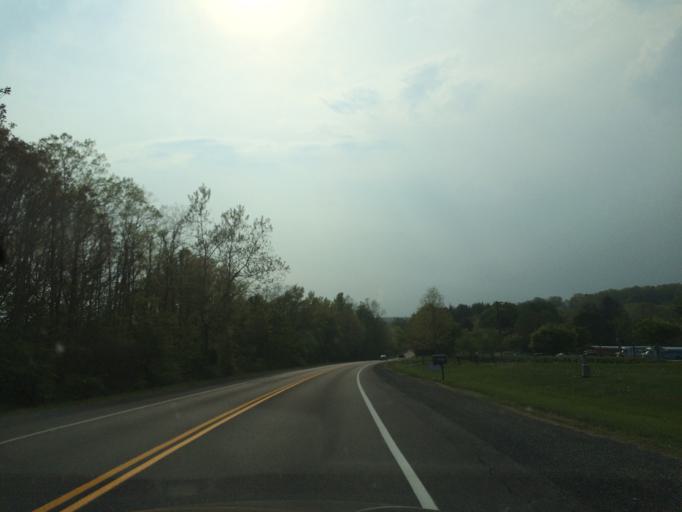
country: US
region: Maryland
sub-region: Carroll County
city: Mount Airy
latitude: 39.3486
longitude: -77.0959
